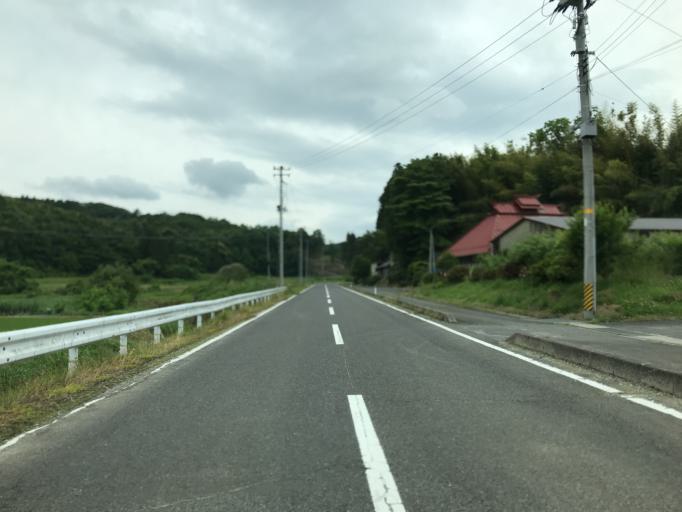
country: JP
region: Fukushima
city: Funehikimachi-funehiki
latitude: 37.4171
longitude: 140.6537
